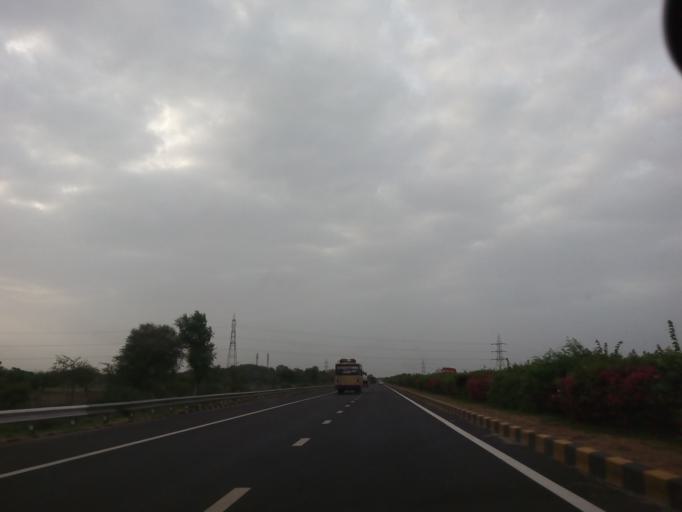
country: IN
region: Gujarat
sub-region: Kheda
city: Mahemdavad
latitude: 22.9398
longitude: 72.7155
